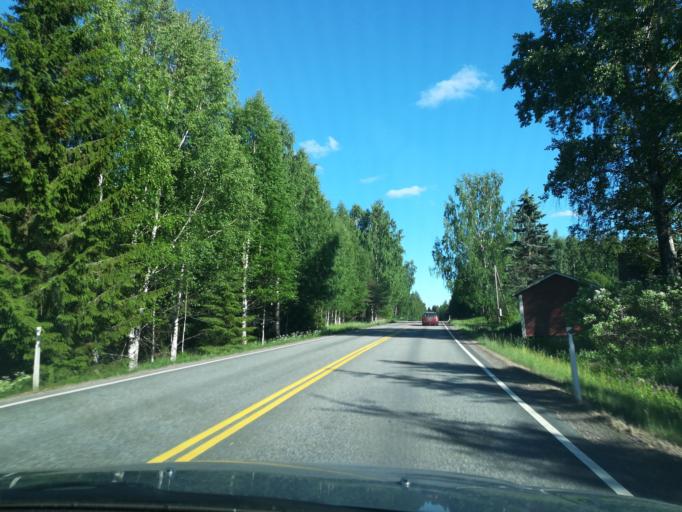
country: FI
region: South Karelia
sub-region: Imatra
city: Ruokolahti
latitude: 61.3706
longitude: 28.6738
